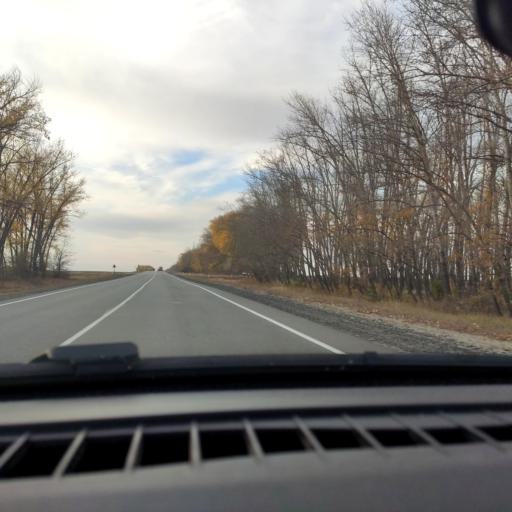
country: RU
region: Voronezj
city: Ostrogozhsk
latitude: 50.9488
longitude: 39.0516
